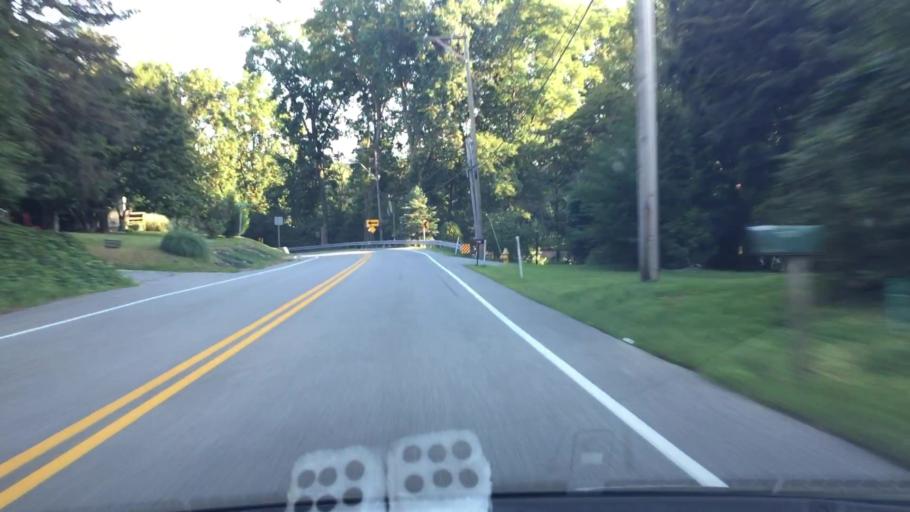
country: US
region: Pennsylvania
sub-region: Delaware County
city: Boothwyn
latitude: 39.8227
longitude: -75.4481
